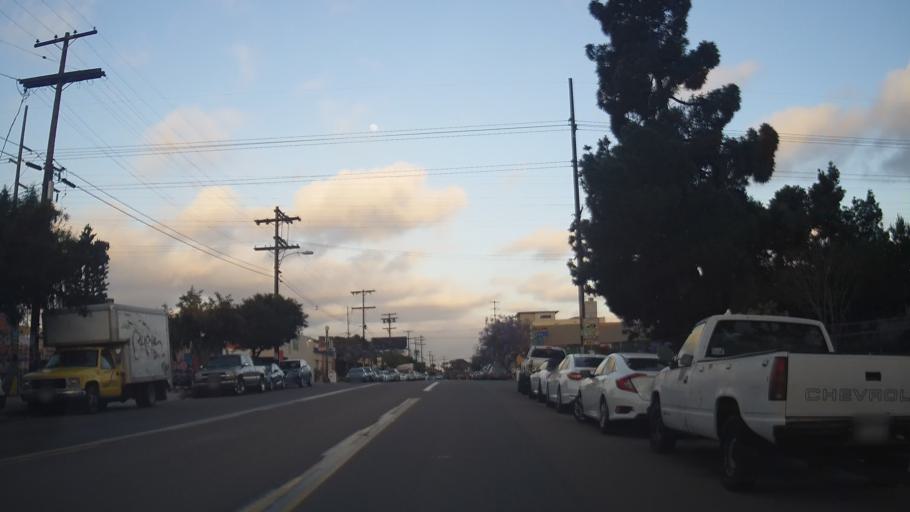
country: US
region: California
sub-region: San Diego County
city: San Diego
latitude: 32.6995
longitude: -117.1415
